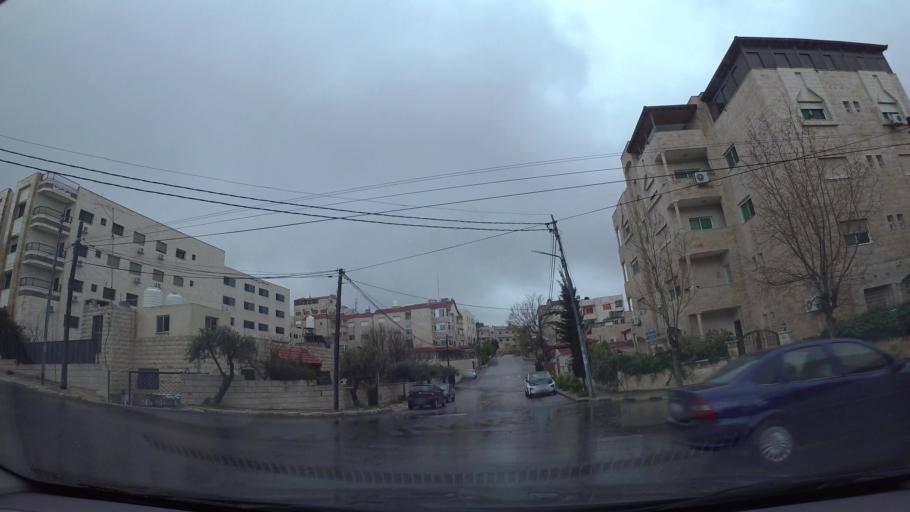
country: JO
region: Amman
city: Al Jubayhah
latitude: 32.0250
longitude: 35.8740
